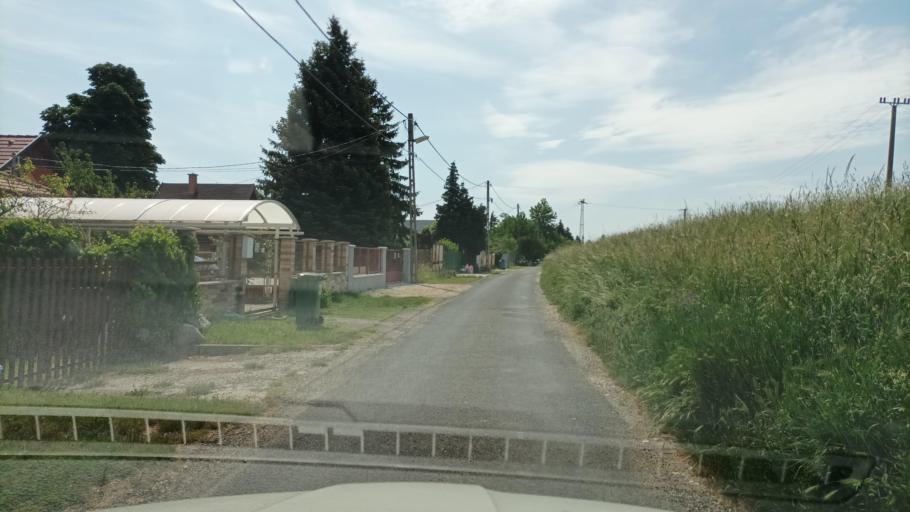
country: HU
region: Pest
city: Rackeve
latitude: 47.1354
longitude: 18.9612
